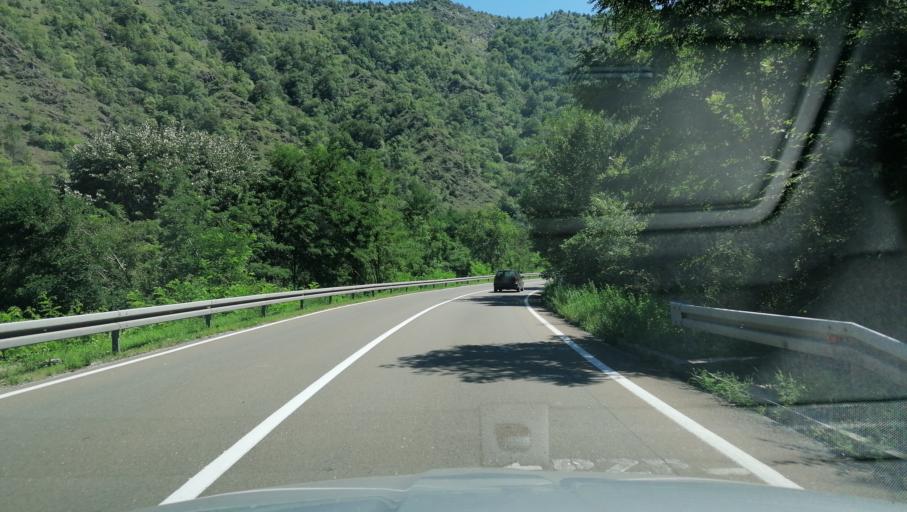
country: RS
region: Central Serbia
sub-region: Raski Okrug
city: Kraljevo
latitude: 43.5604
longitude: 20.6181
